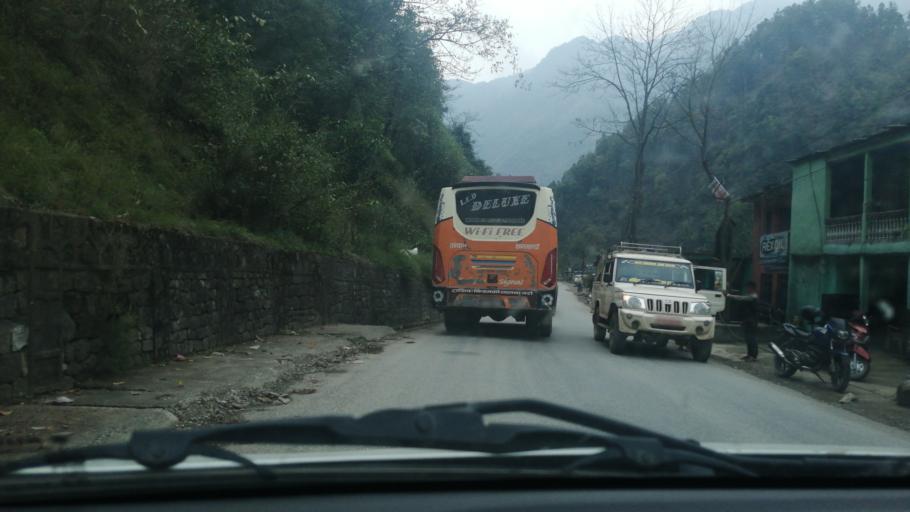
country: NP
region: Western Region
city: Tansen
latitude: 27.8068
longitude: 83.5149
